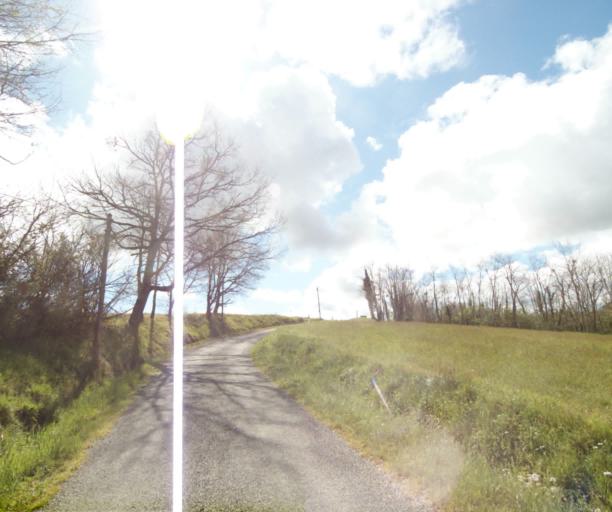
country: FR
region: Midi-Pyrenees
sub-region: Departement de l'Ariege
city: Saverdun
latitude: 43.2018
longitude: 1.5844
